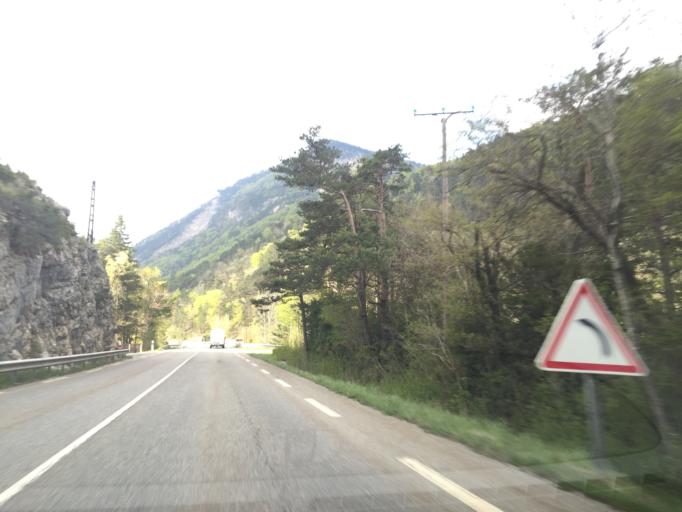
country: FR
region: Provence-Alpes-Cote d'Azur
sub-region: Departement des Hautes-Alpes
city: Veynes
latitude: 44.6130
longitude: 5.7086
